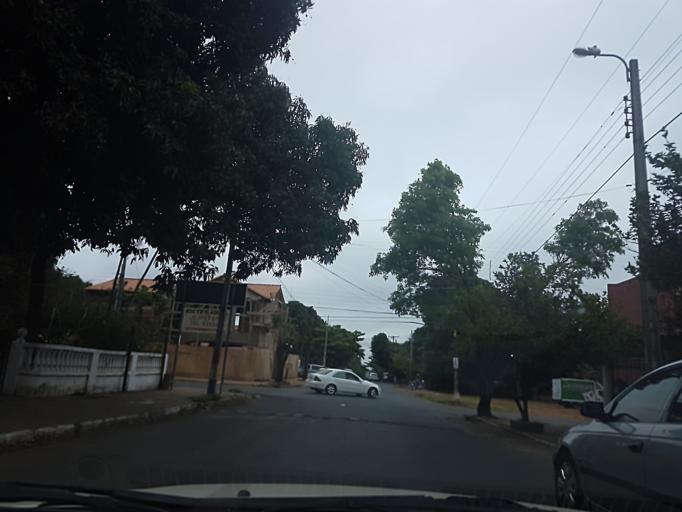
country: PY
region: Central
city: Lambare
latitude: -25.3339
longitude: -57.5725
